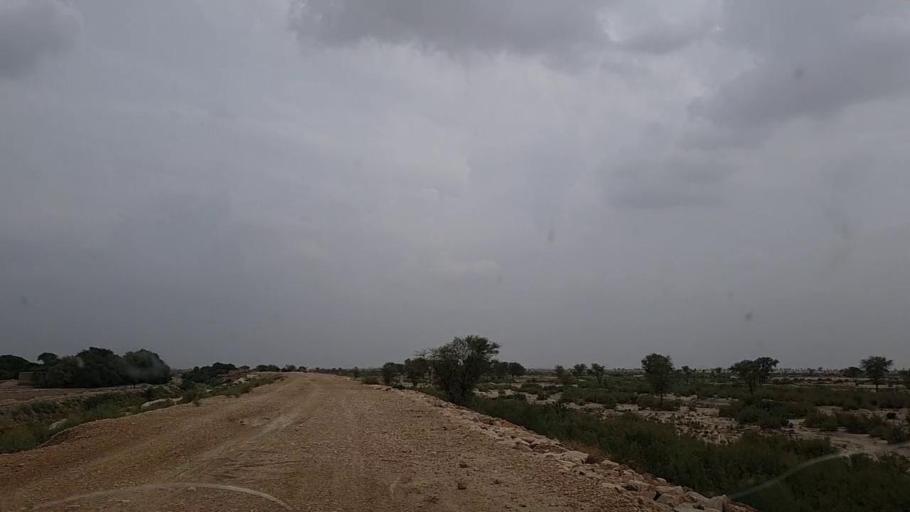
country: PK
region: Sindh
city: Johi
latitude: 26.7230
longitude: 67.5784
